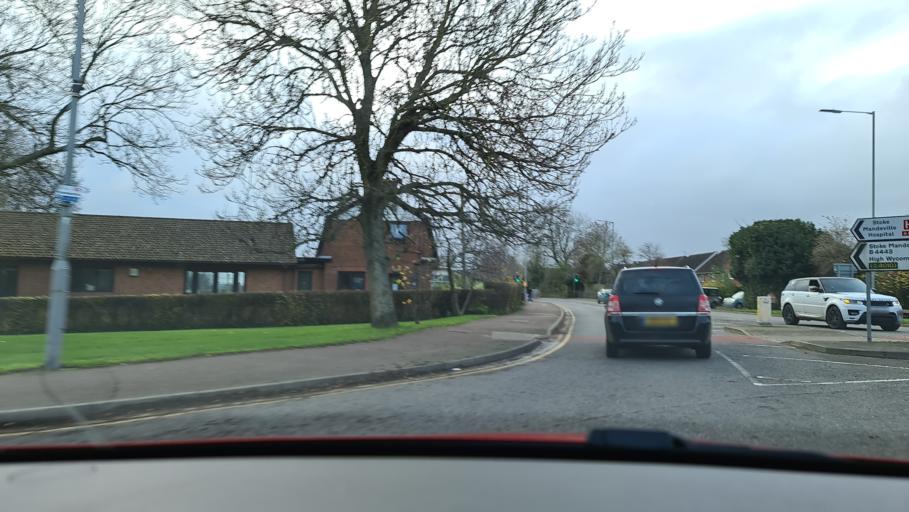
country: GB
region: England
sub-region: Buckinghamshire
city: Aylesbury
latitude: 51.7981
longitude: -0.8054
